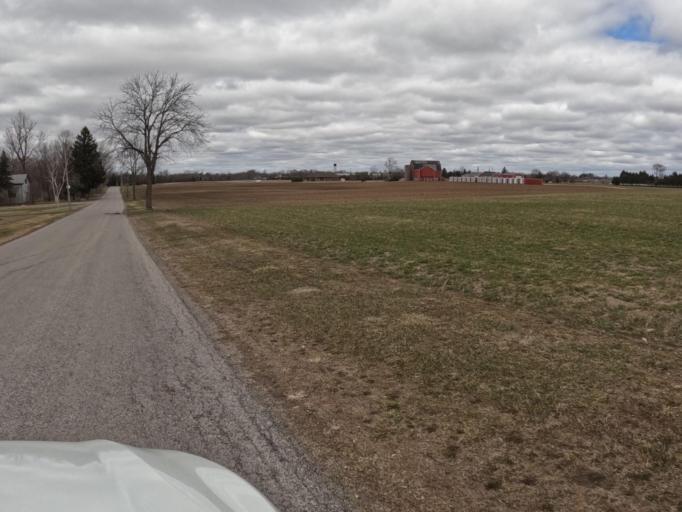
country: CA
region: Ontario
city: Norfolk County
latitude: 42.8348
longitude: -80.4987
